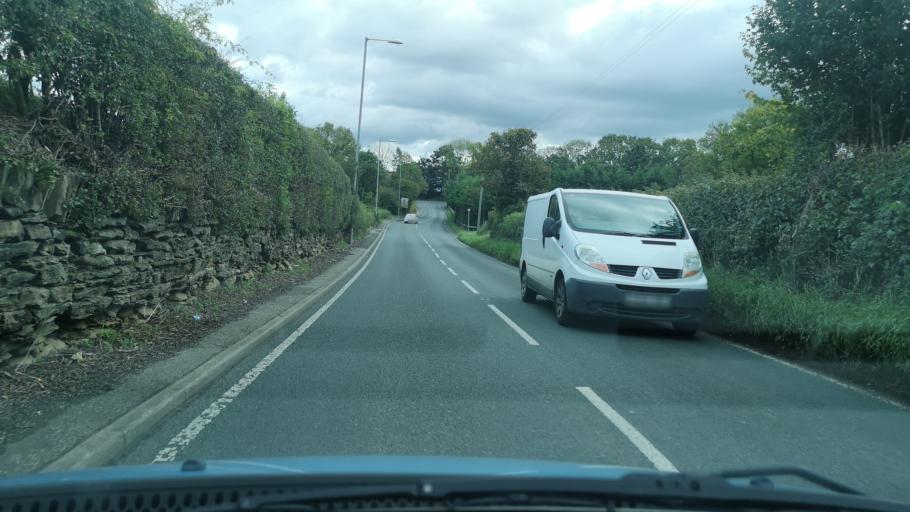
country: GB
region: England
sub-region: City and Borough of Wakefield
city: Middlestown
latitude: 53.6571
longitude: -1.5845
